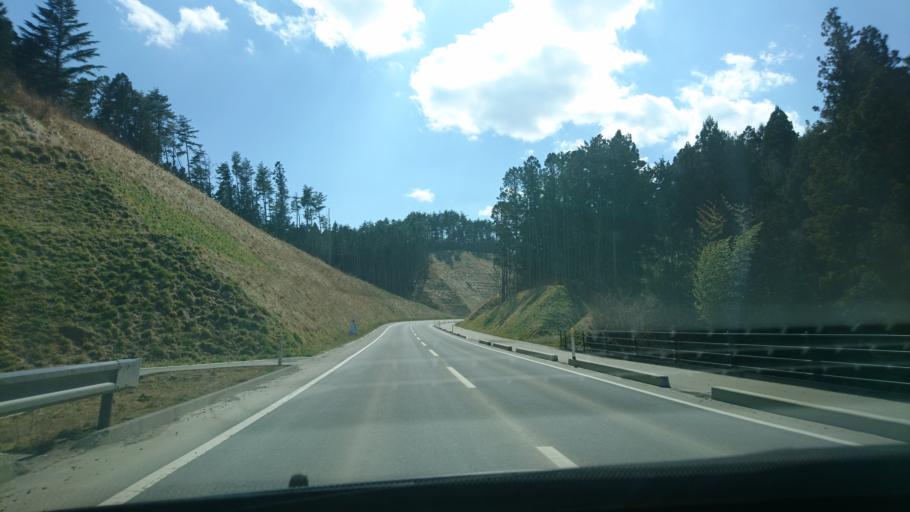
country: JP
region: Miyagi
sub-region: Oshika Gun
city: Onagawa Cho
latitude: 38.6398
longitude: 141.4495
